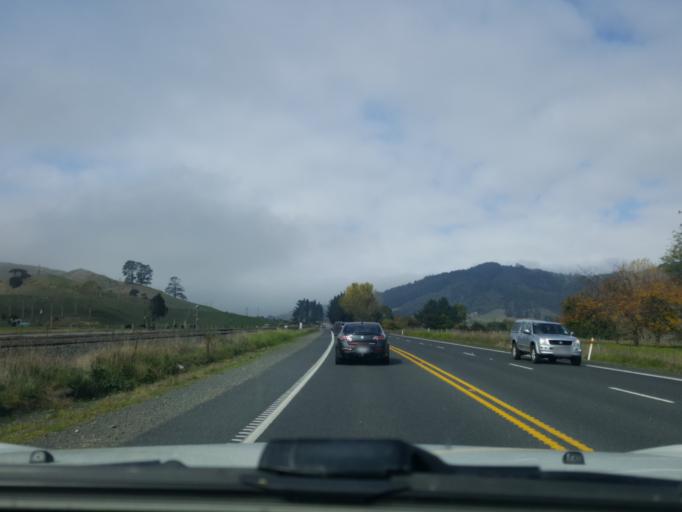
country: NZ
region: Waikato
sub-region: Waikato District
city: Ngaruawahia
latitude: -37.5938
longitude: 175.1603
